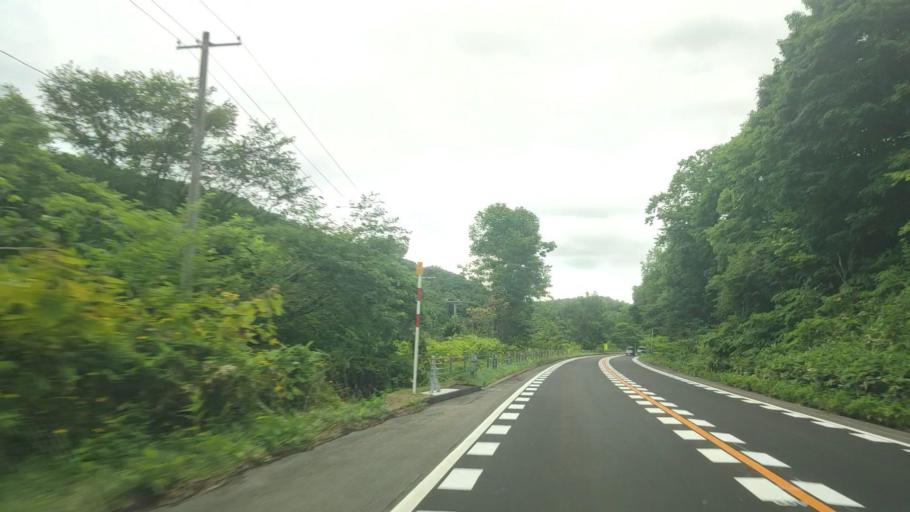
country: JP
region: Hokkaido
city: Niseko Town
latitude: 42.6003
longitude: 140.6077
